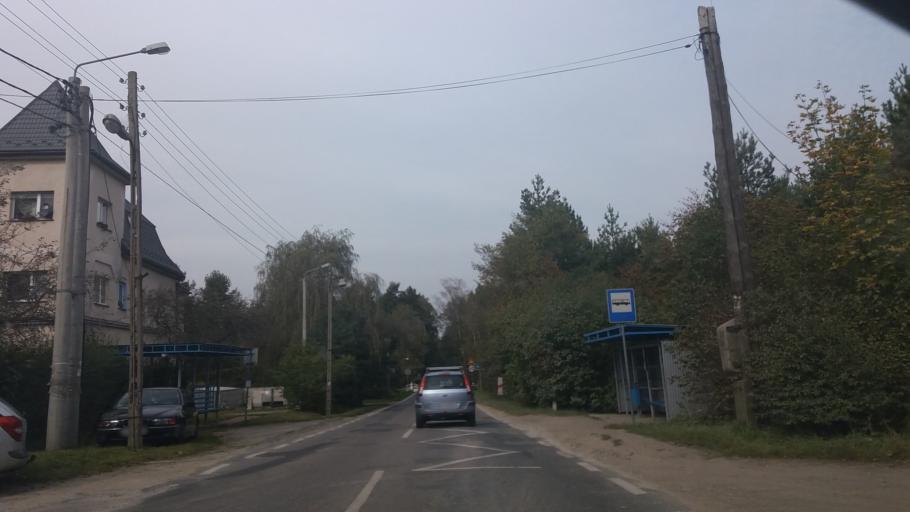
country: PL
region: Lesser Poland Voivodeship
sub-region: Powiat chrzanowski
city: Pogorzyce
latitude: 50.1127
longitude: 19.4427
